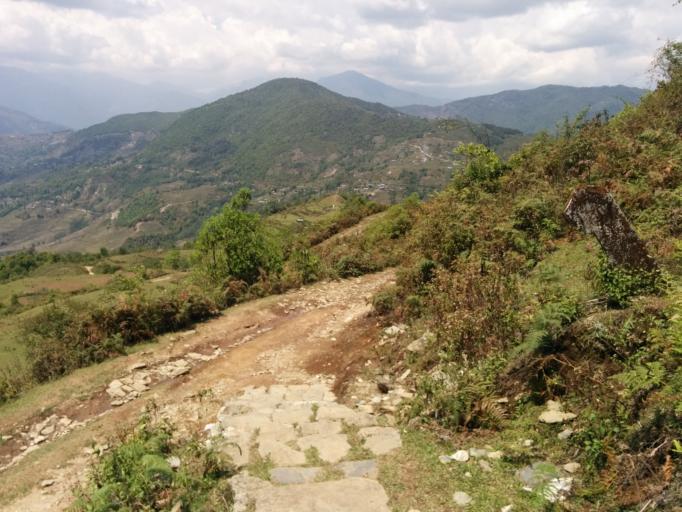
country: NP
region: Western Region
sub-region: Gandaki Zone
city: Pokhara
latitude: 28.2562
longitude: 83.8224
